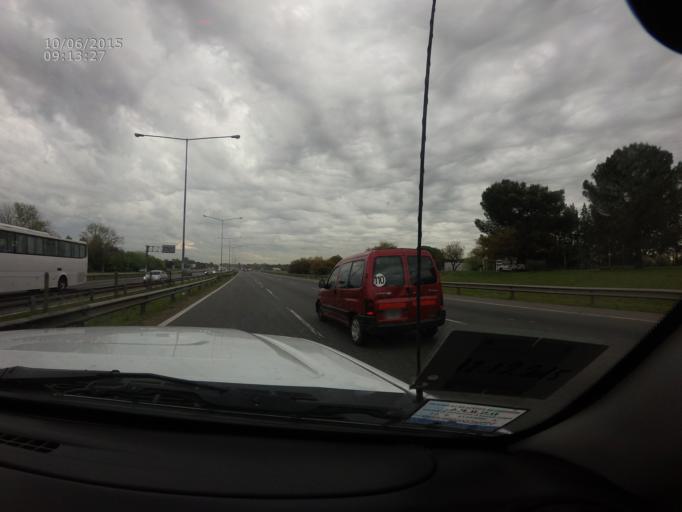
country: AR
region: Buenos Aires
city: Belen de Escobar
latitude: -34.3378
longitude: -58.8190
